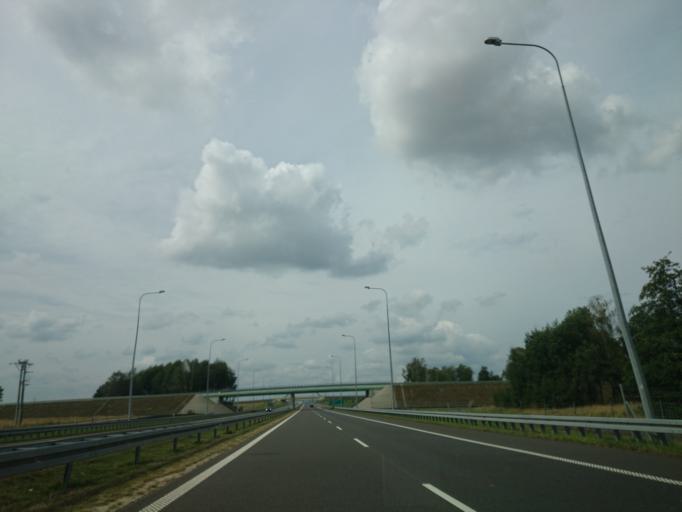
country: PL
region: West Pomeranian Voivodeship
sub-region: Powiat pyrzycki
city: Kozielice
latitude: 53.1179
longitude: 14.7459
